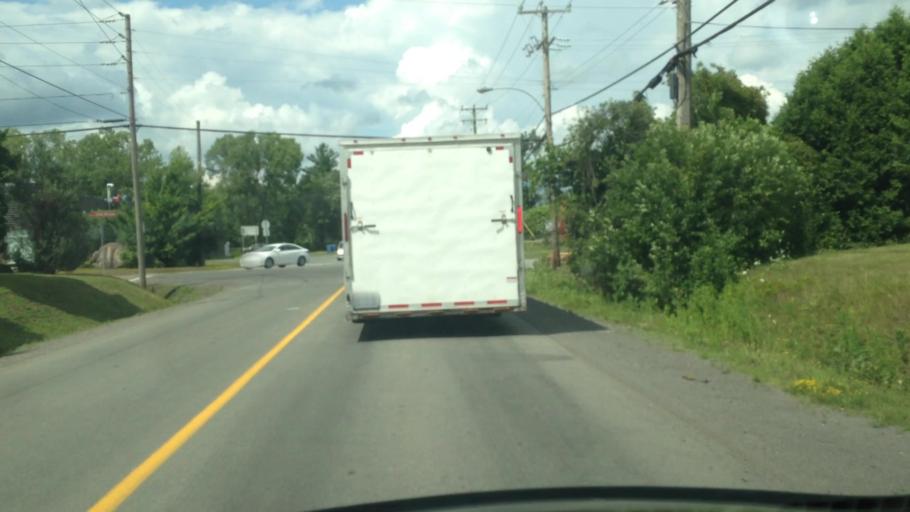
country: CA
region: Quebec
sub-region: Laurentides
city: Saint-Jerome
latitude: 45.7688
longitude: -74.0228
